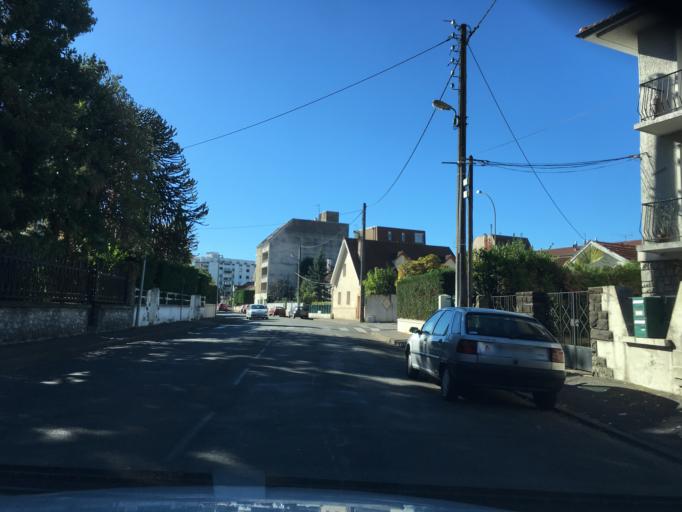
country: FR
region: Aquitaine
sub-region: Departement des Pyrenees-Atlantiques
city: Pau
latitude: 43.3054
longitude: -0.3569
